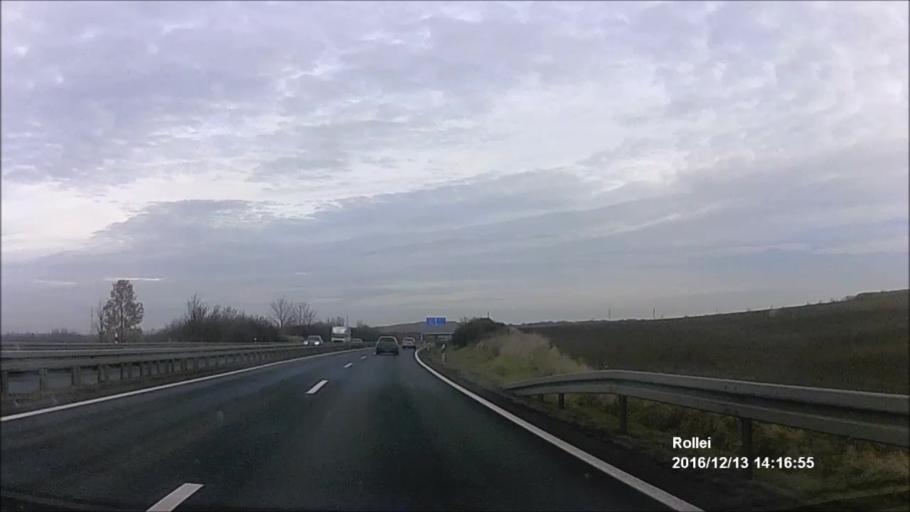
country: DE
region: Thuringia
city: Erfurt
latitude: 51.0244
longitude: 11.0586
